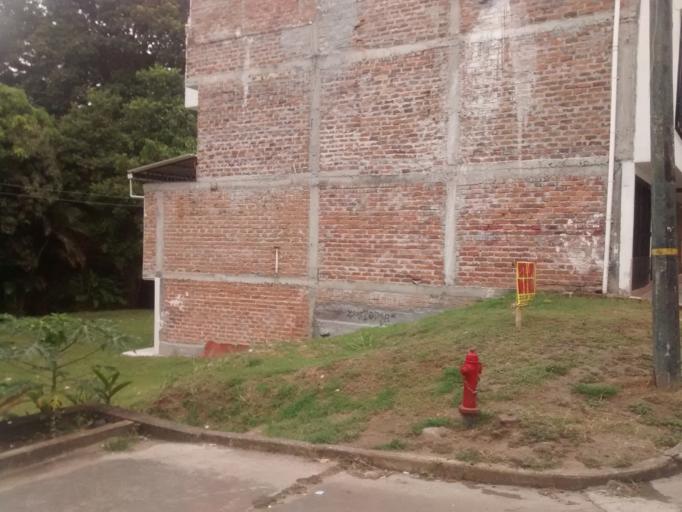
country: CO
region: Tolima
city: Ibague
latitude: 4.4469
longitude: -75.2004
